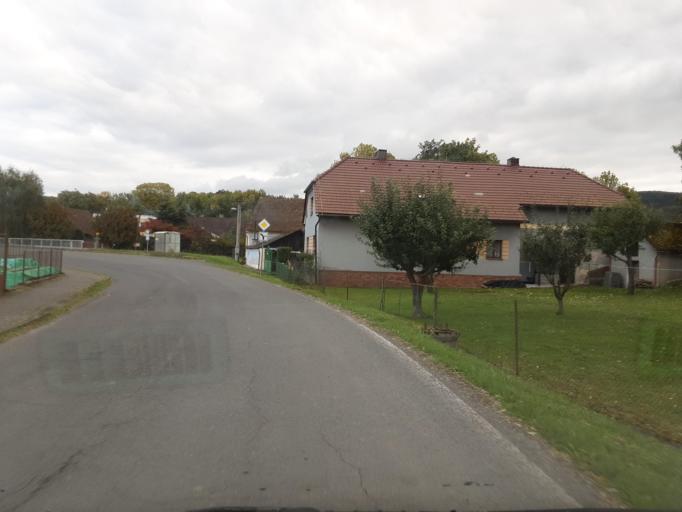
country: CZ
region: Plzensky
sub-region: Okres Domazlice
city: Kdyne
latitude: 49.3970
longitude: 13.1289
